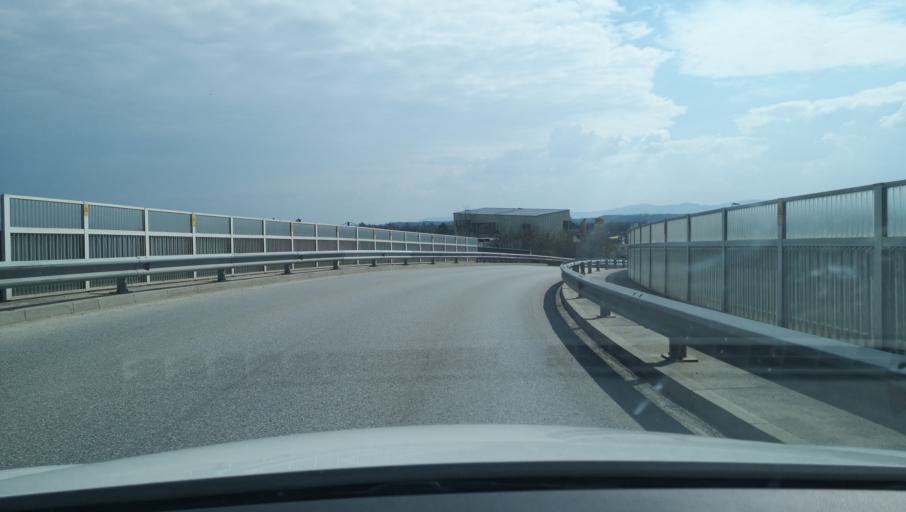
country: AT
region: Lower Austria
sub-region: Politischer Bezirk Amstetten
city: Winklarn
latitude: 48.1031
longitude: 14.8217
